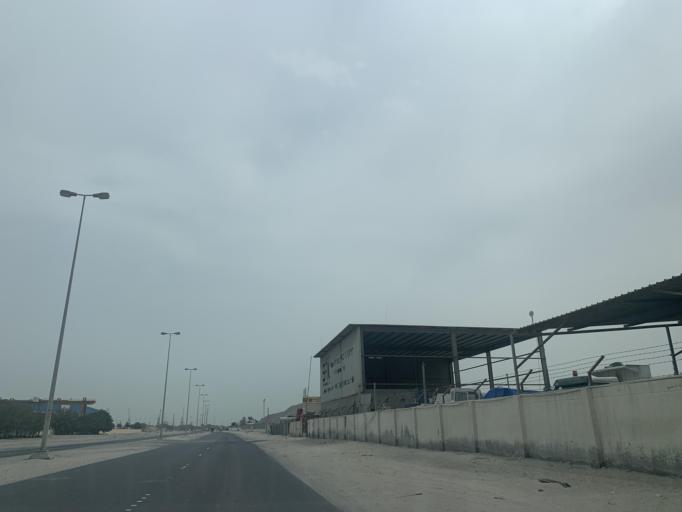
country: BH
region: Muharraq
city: Al Hadd
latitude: 26.2082
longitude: 50.6589
